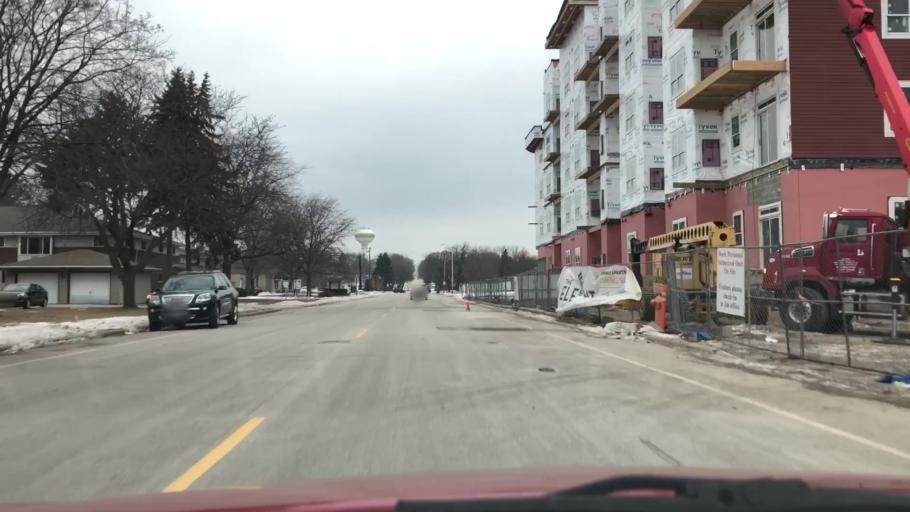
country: US
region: Wisconsin
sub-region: Brown County
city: Ashwaubenon
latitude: 44.4914
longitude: -88.0595
